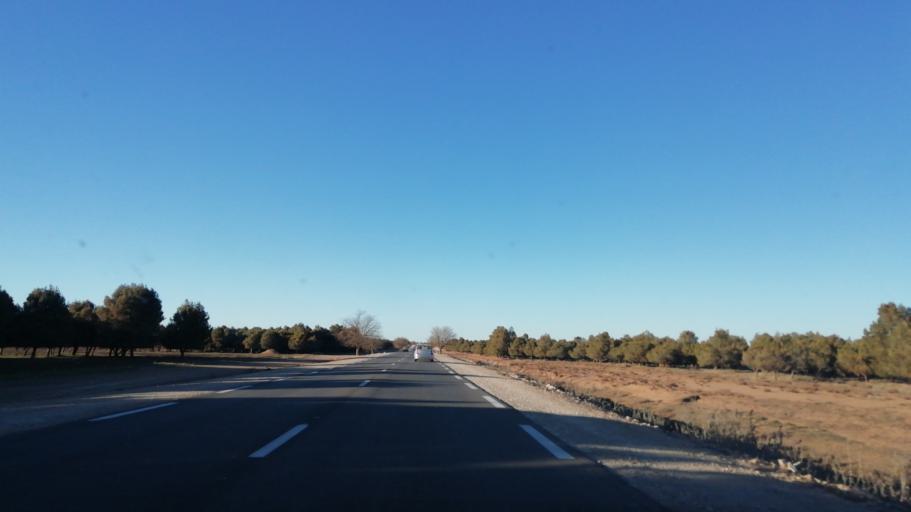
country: DZ
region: Tlemcen
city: Sebdou
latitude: 34.5103
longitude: -1.2827
